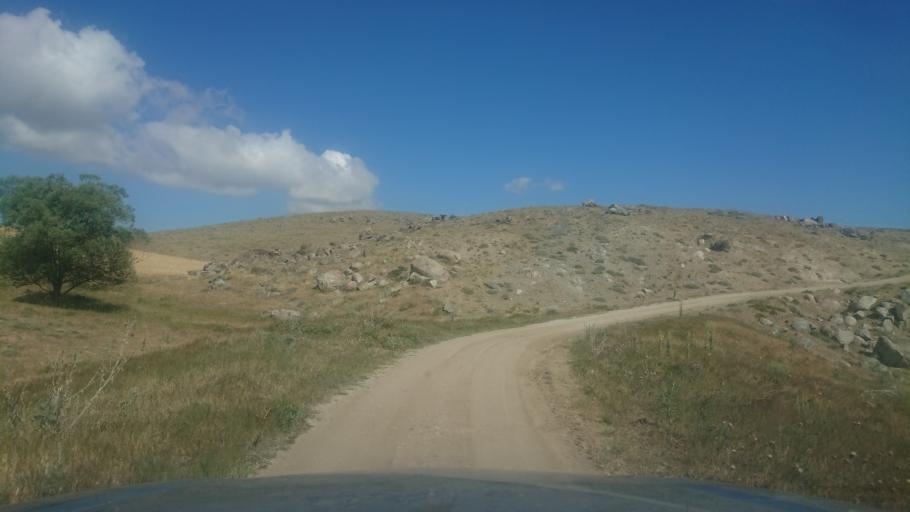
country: TR
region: Aksaray
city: Sariyahsi
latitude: 38.9197
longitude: 33.8527
